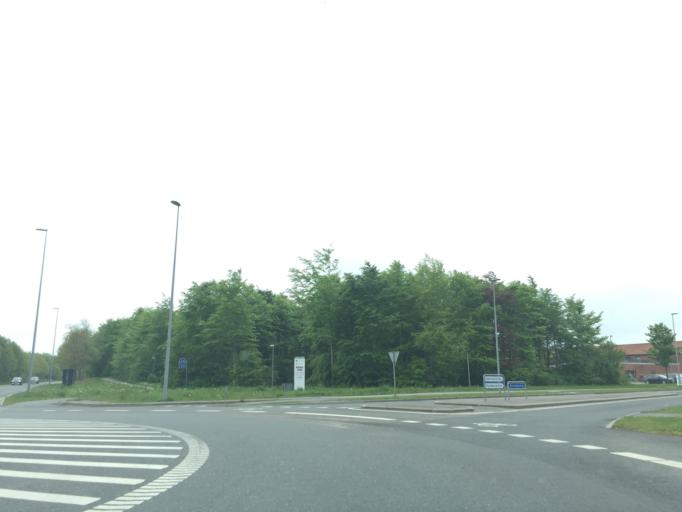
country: DK
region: Central Jutland
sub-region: Silkeborg Kommune
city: Silkeborg
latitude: 56.1951
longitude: 9.6019
